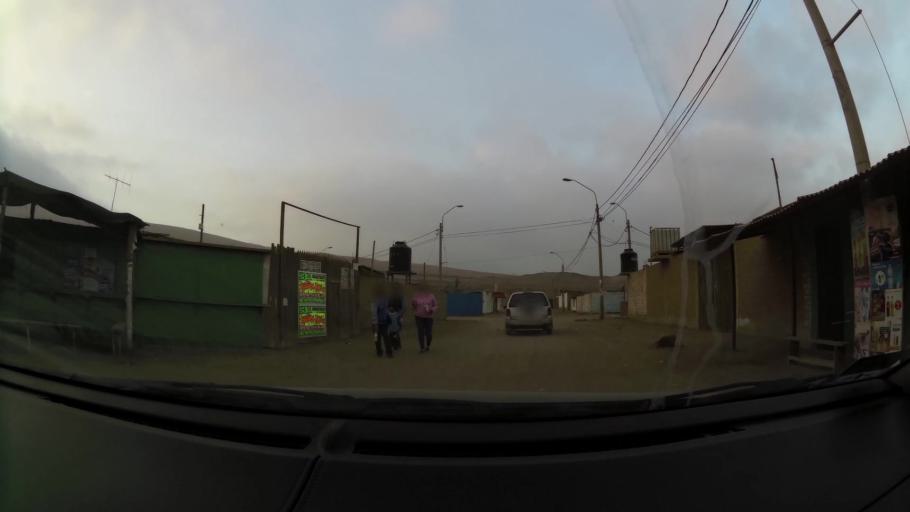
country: PE
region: Lima
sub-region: Lima
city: Santa Rosa
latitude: -11.7329
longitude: -77.1411
